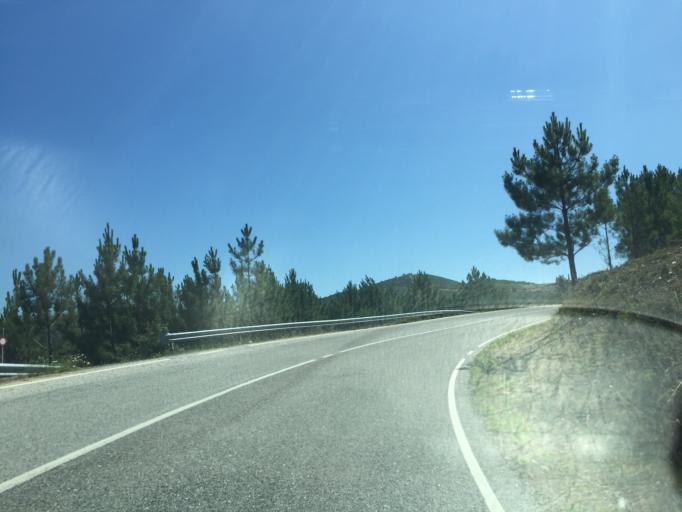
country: PT
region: Coimbra
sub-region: Pampilhosa da Serra
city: Pampilhosa da Serra
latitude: 40.1268
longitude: -7.8103
